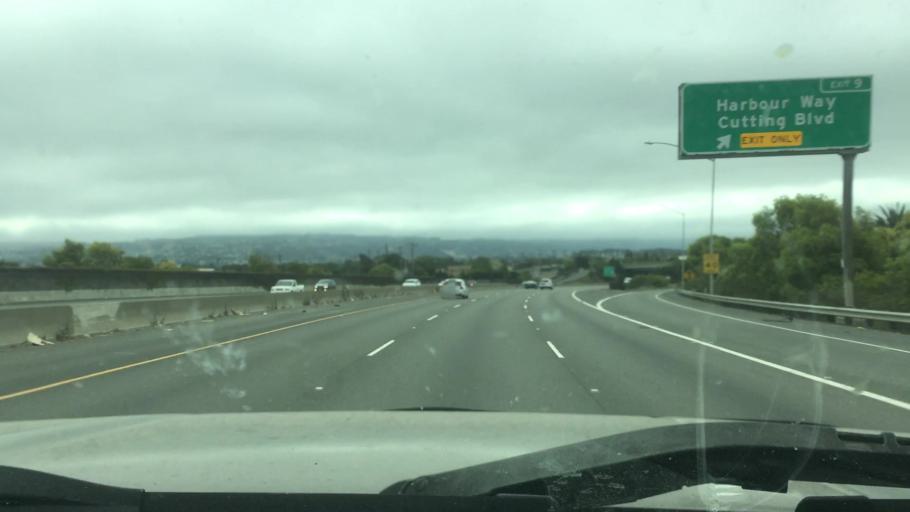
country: US
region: California
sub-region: Contra Costa County
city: Richmond
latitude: 37.9268
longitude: -122.3673
